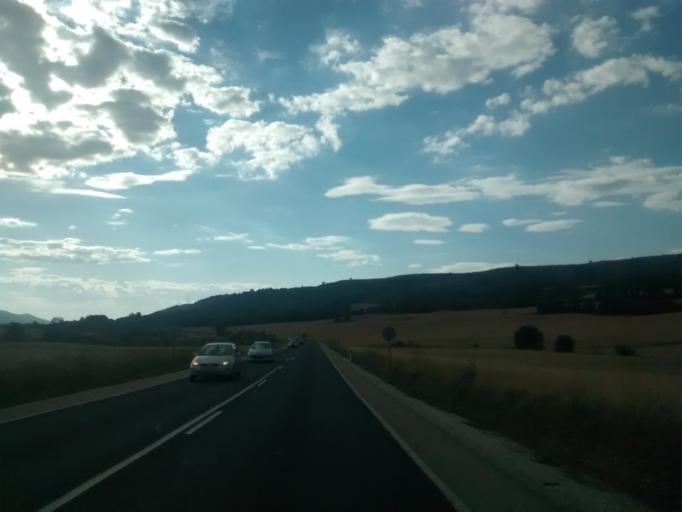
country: ES
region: Castille and Leon
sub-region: Provincia de Burgos
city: Basconcillos del Tozo
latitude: 42.6801
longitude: -3.9477
